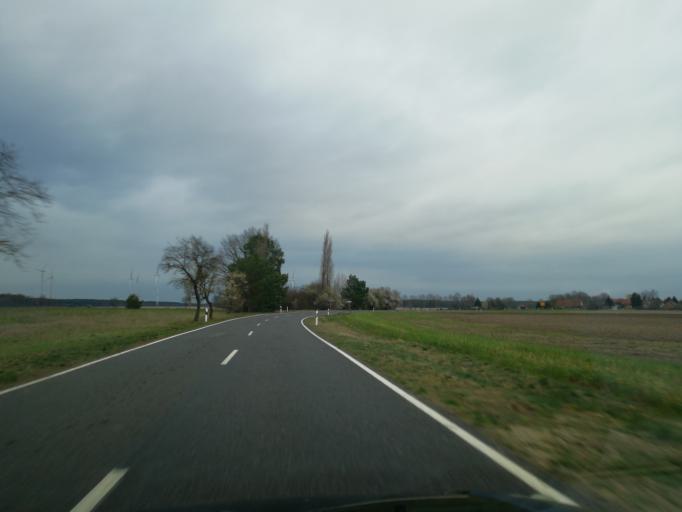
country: DE
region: Brandenburg
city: Vetschau
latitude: 51.7337
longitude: 14.1081
